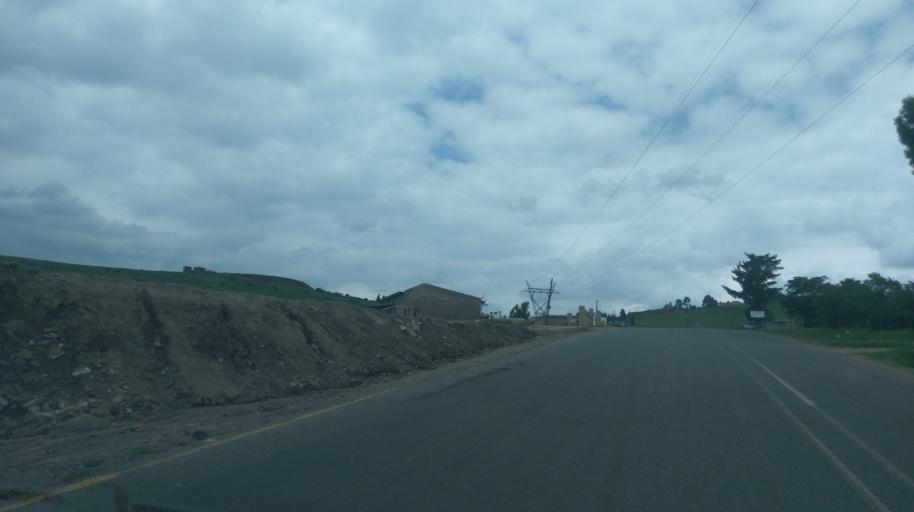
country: LS
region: Leribe
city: Leribe
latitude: -28.9938
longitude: 28.1950
